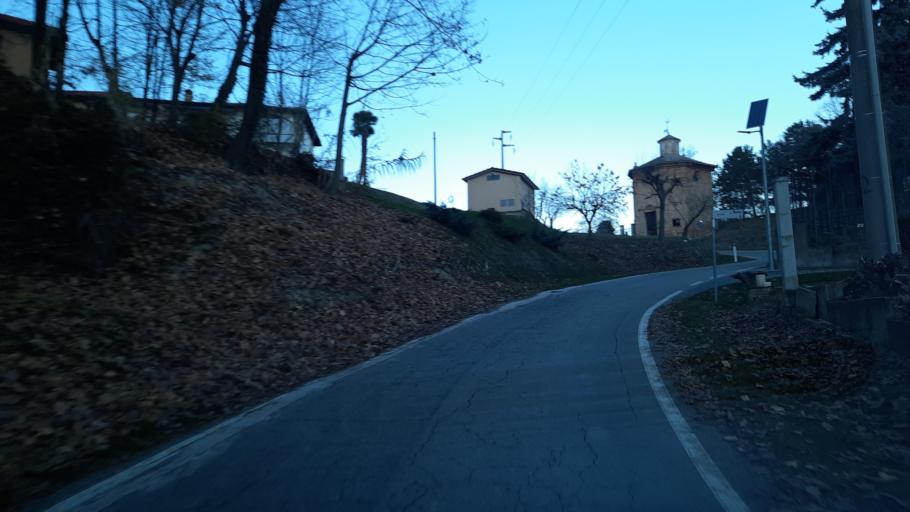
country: IT
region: Piedmont
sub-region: Provincia di Alessandria
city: Camino
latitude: 45.1622
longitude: 8.2834
